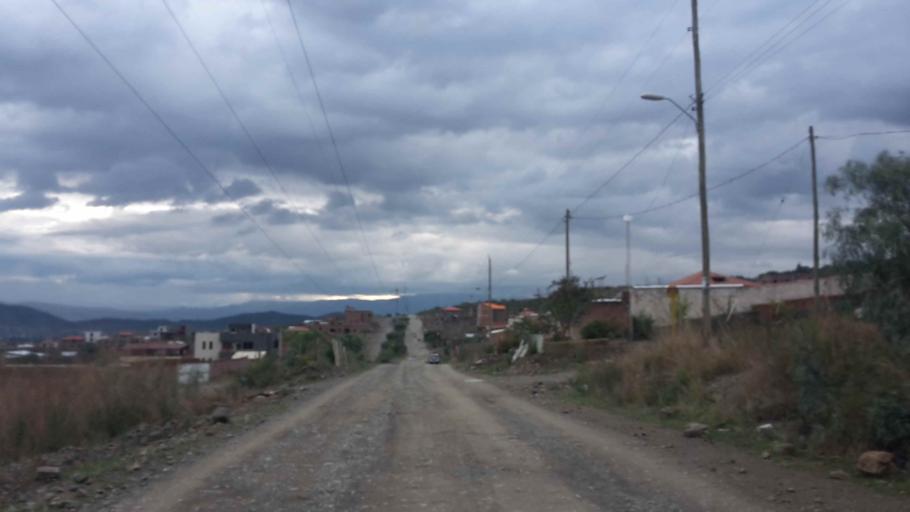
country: BO
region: Cochabamba
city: Cochabamba
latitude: -17.3782
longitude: -66.0629
